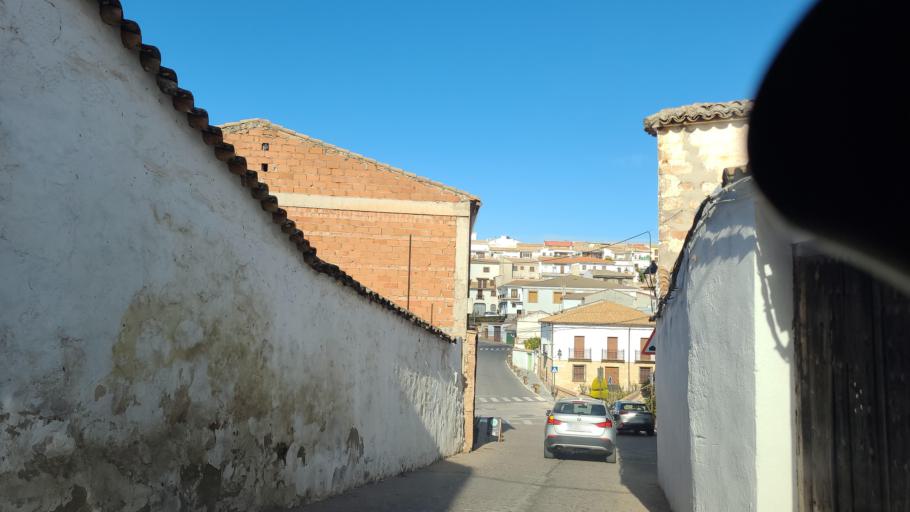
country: ES
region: Andalusia
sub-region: Provincia de Jaen
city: Banos de la Encina
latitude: 38.1712
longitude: -3.7749
